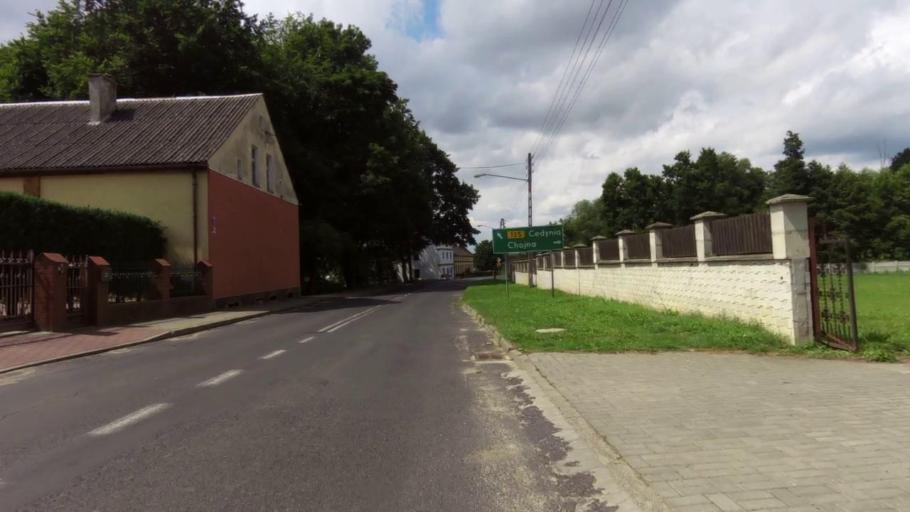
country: PL
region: West Pomeranian Voivodeship
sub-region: Powiat gryfinski
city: Moryn
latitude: 52.8597
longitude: 14.3886
